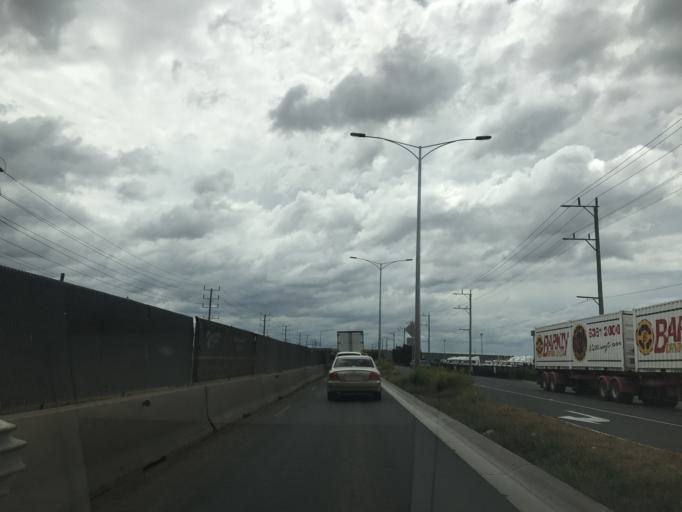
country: AU
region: Victoria
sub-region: Wyndham
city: Truganina
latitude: -37.8026
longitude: 144.7519
